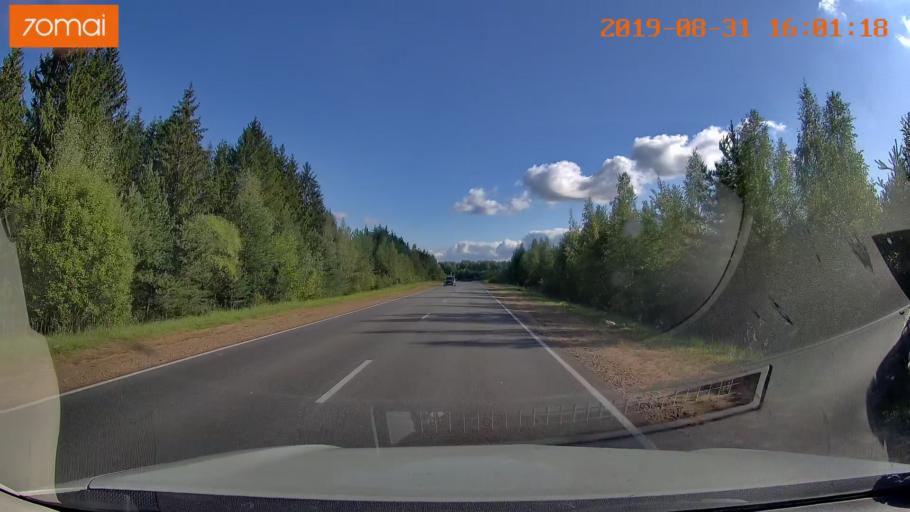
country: RU
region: Kaluga
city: Yukhnov
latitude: 54.6919
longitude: 35.2892
